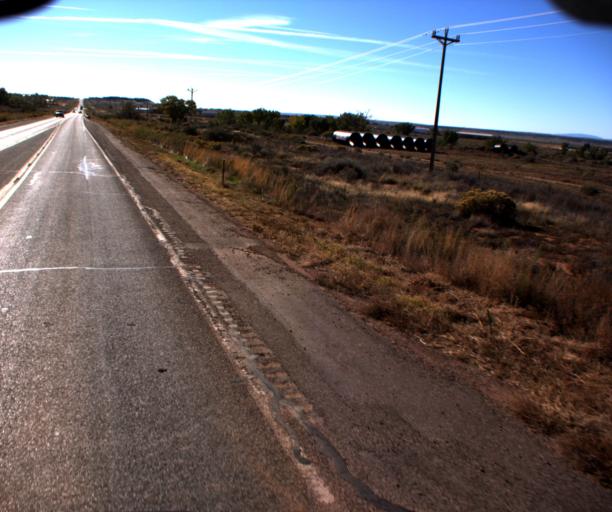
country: US
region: Arizona
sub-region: Mohave County
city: Colorado City
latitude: 36.9903
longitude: -112.9910
